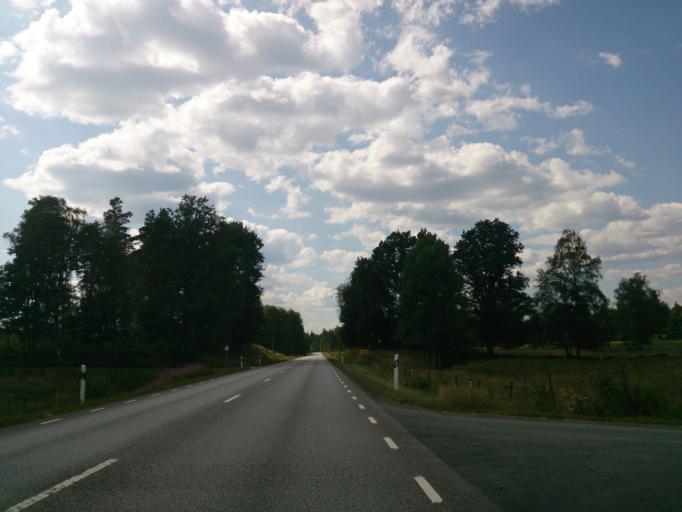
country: SE
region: Joenkoeping
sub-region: Gislaveds Kommun
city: Reftele
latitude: 57.1574
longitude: 13.5108
